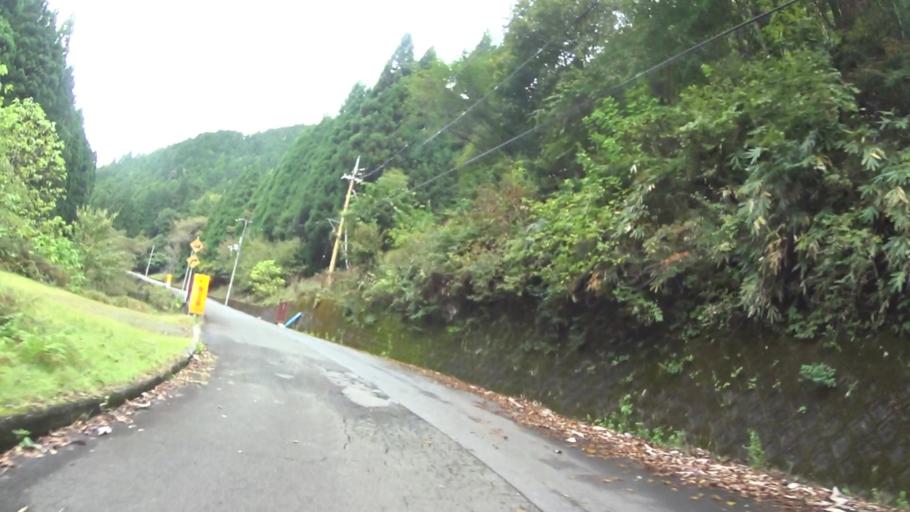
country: JP
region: Shiga Prefecture
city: Kitahama
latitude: 35.2676
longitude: 135.7406
